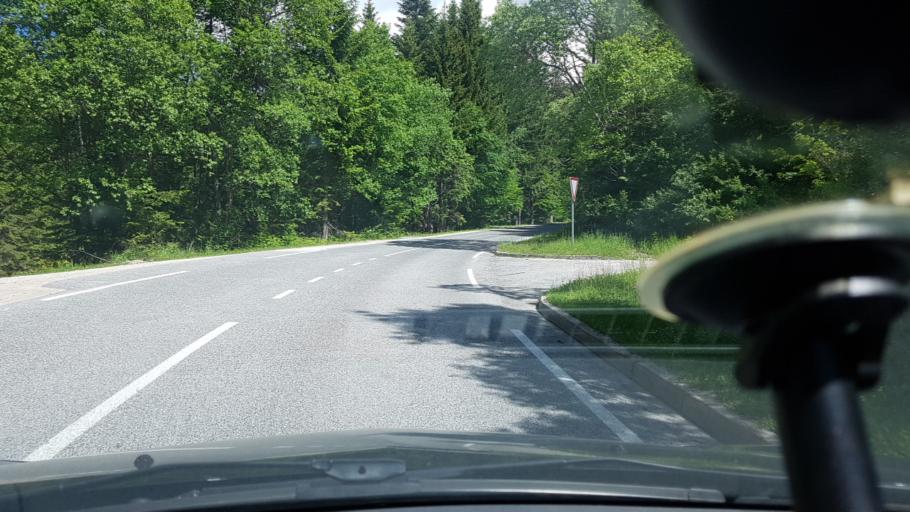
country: SI
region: Zrece
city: Zrece
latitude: 46.4395
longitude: 15.3643
